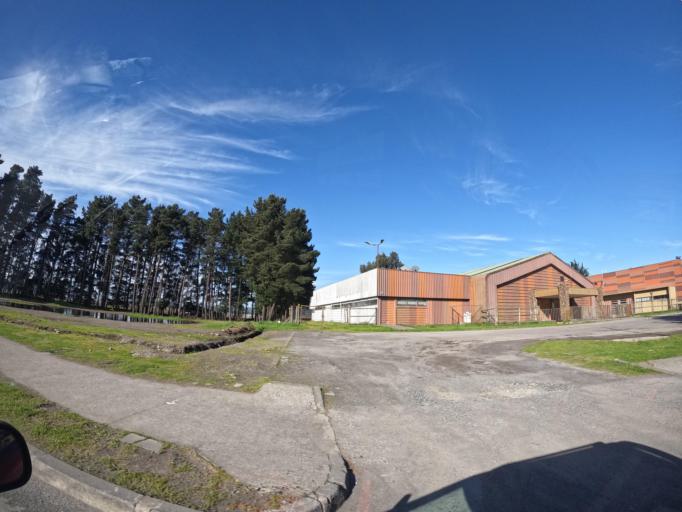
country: CL
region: Biobio
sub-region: Provincia de Concepcion
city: Concepcion
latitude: -36.7748
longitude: -73.0689
